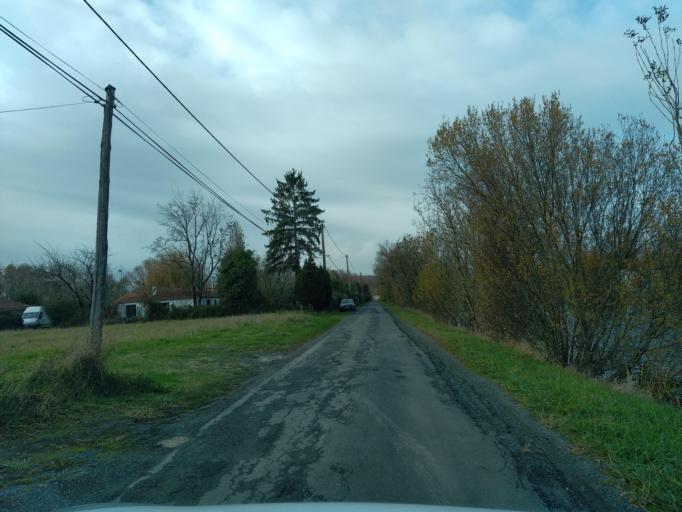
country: FR
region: Pays de la Loire
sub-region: Departement de la Vendee
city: Vix
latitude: 46.3338
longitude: -0.8092
